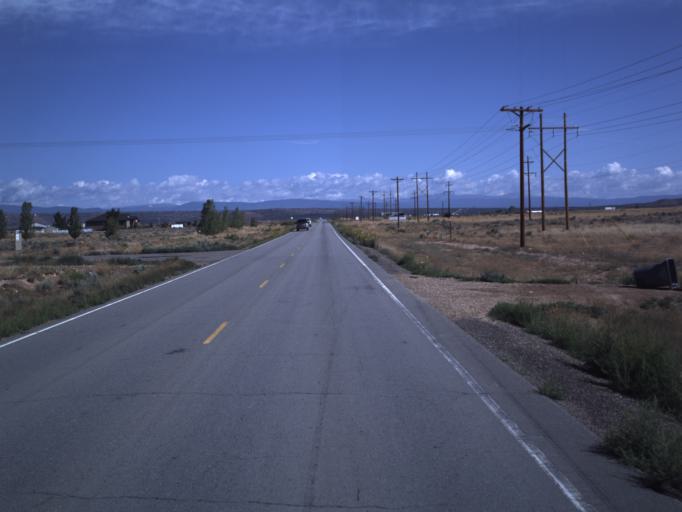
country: US
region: Utah
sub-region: Duchesne County
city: Duchesne
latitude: 40.2169
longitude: -110.3893
